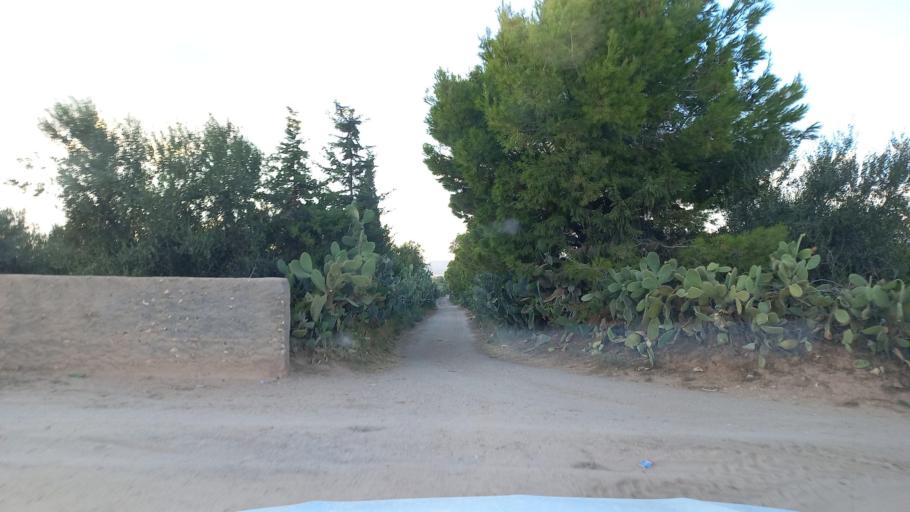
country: TN
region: Al Qasrayn
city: Sbiba
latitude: 35.3777
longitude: 9.0556
